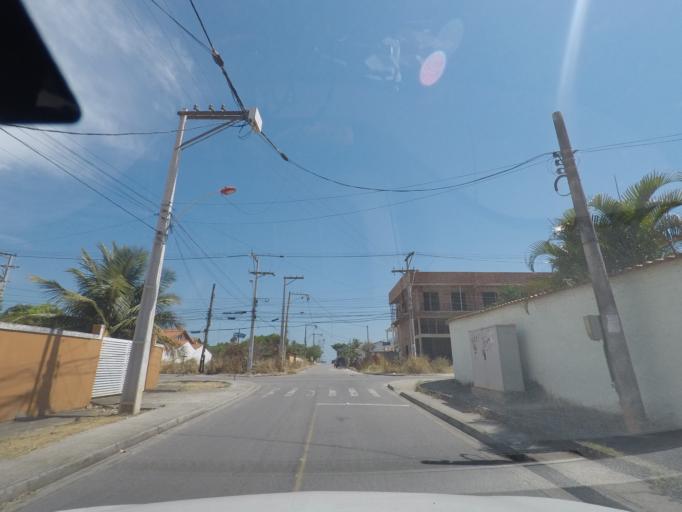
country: BR
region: Rio de Janeiro
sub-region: Marica
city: Marica
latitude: -22.9644
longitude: -42.9594
